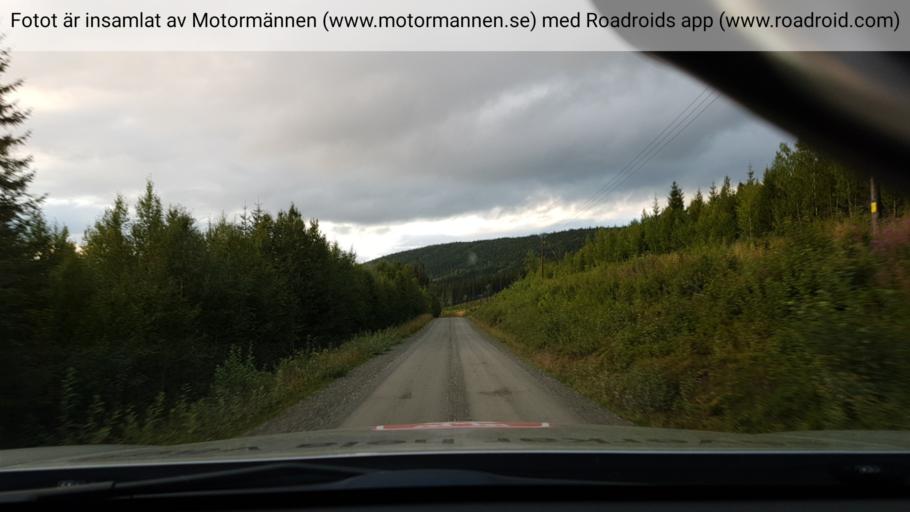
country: SE
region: Vaesterbotten
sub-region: Vilhelmina Kommun
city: Sjoberg
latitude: 65.5925
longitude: 15.2849
